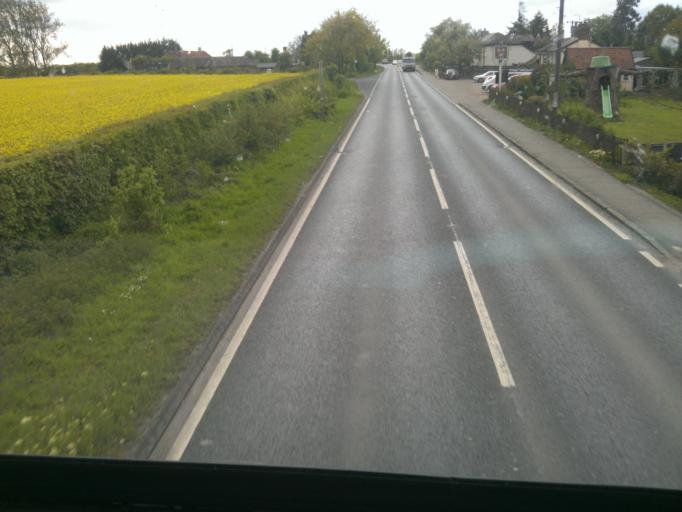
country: GB
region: England
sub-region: Essex
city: Marks Tey
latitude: 51.8755
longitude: 0.7294
